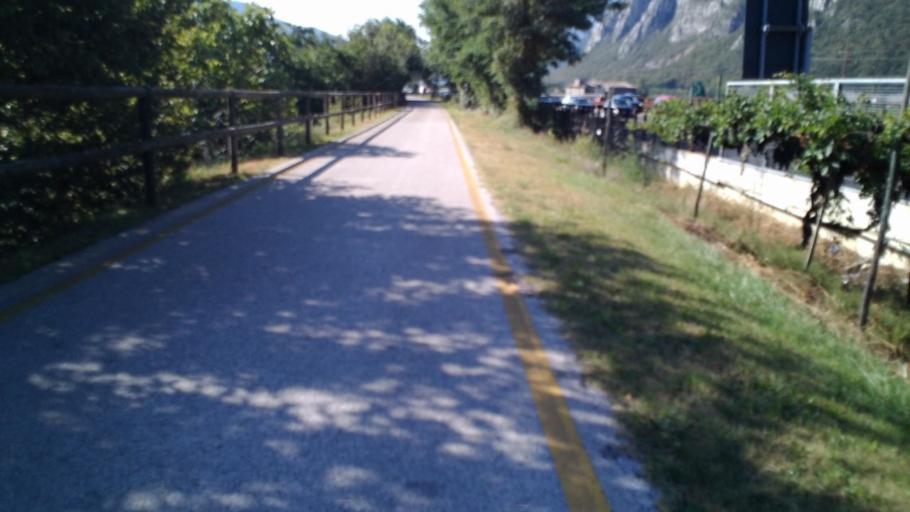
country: IT
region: Trentino-Alto Adige
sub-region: Provincia di Trento
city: Avio
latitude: 45.7221
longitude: 10.9370
